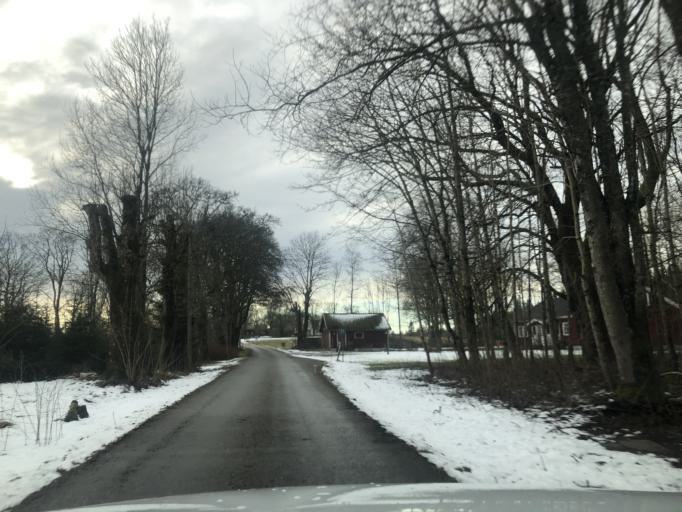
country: SE
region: Vaestra Goetaland
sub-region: Ulricehamns Kommun
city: Ulricehamn
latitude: 57.8086
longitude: 13.5126
